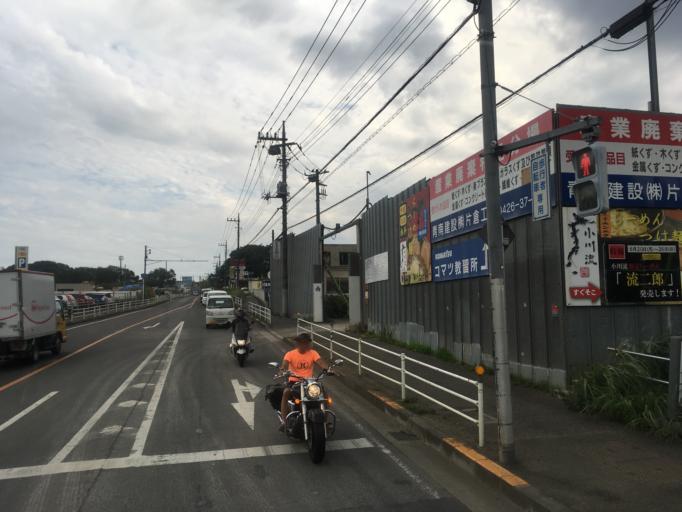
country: JP
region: Tokyo
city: Hachioji
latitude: 35.6307
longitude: 139.3381
